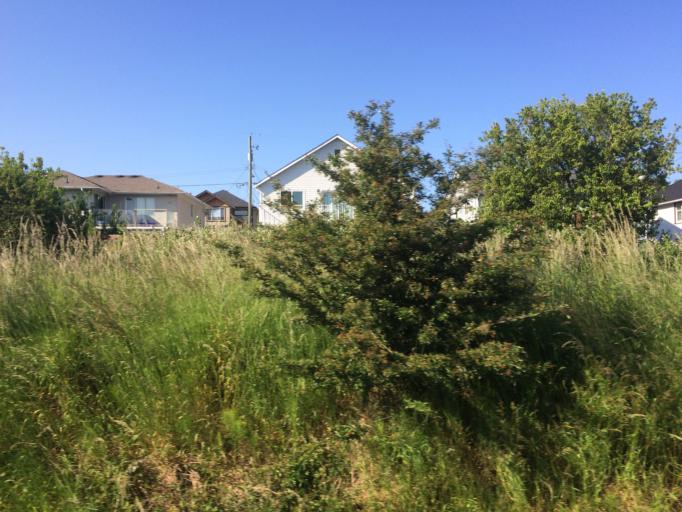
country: CA
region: British Columbia
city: Victoria
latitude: 48.4577
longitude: -123.3883
